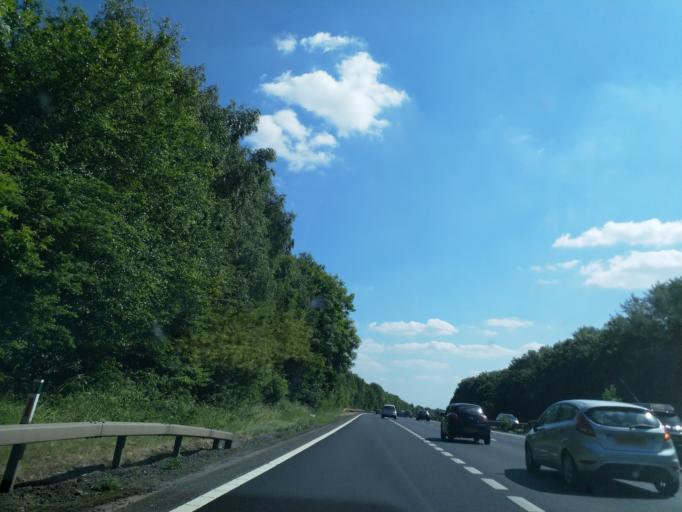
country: GB
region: England
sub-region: Warwickshire
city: Kenilworth
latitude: 52.3189
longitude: -1.5696
